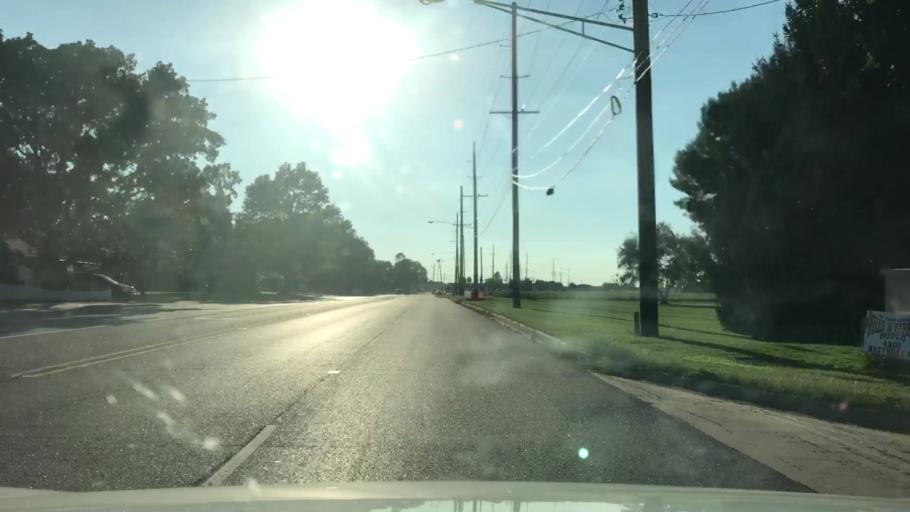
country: US
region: Illinois
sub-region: Madison County
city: Granite City
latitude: 38.7316
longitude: -90.1313
